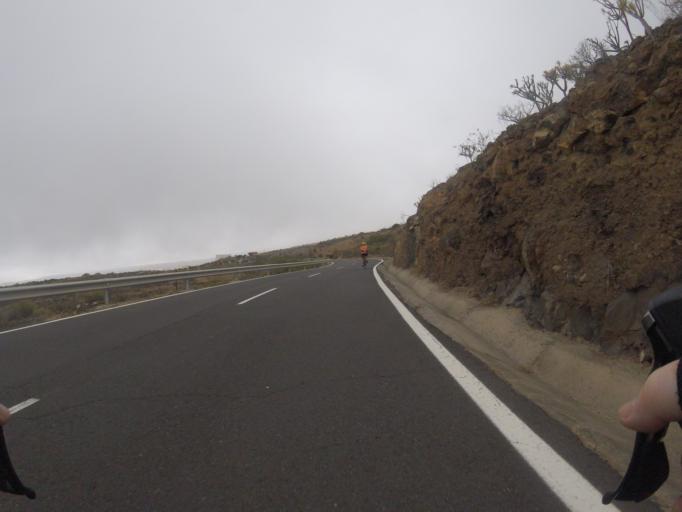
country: ES
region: Canary Islands
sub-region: Provincia de Santa Cruz de Tenerife
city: Lomo de Arico
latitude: 28.1998
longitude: -16.4659
